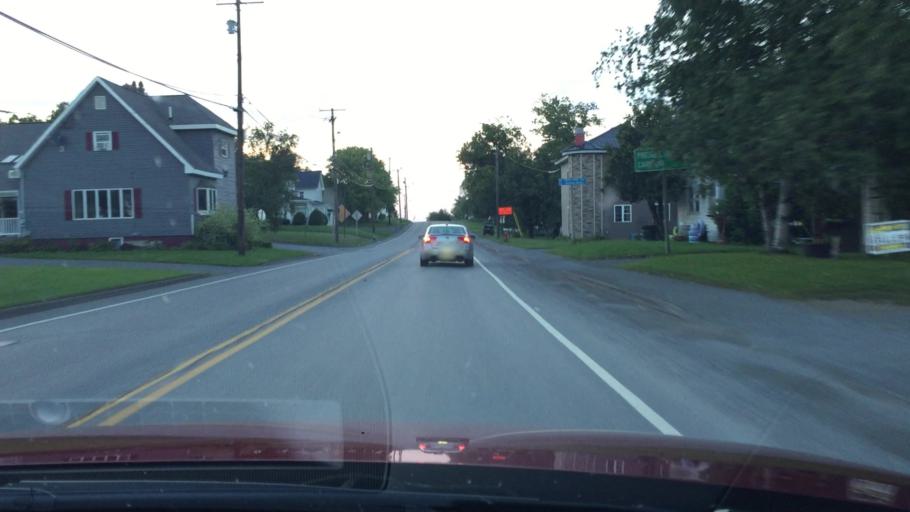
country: US
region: Maine
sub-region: Aroostook County
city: Easton
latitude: 46.5165
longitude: -67.8677
